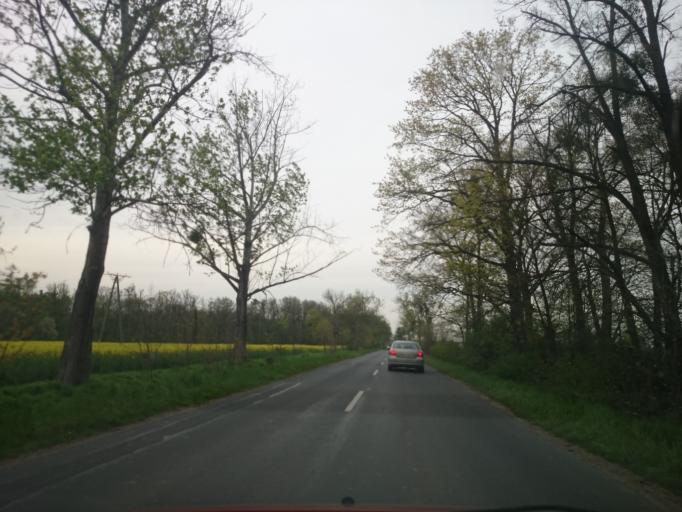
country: PL
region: Opole Voivodeship
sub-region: Powiat brzeski
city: Grodkow
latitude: 50.6503
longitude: 17.4397
